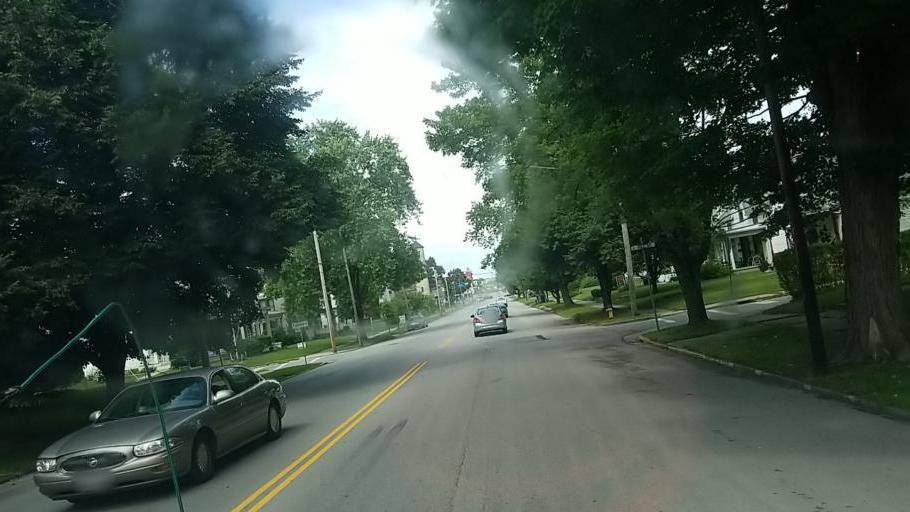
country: US
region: Ohio
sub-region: Champaign County
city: Urbana
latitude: 40.1030
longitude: -83.7530
